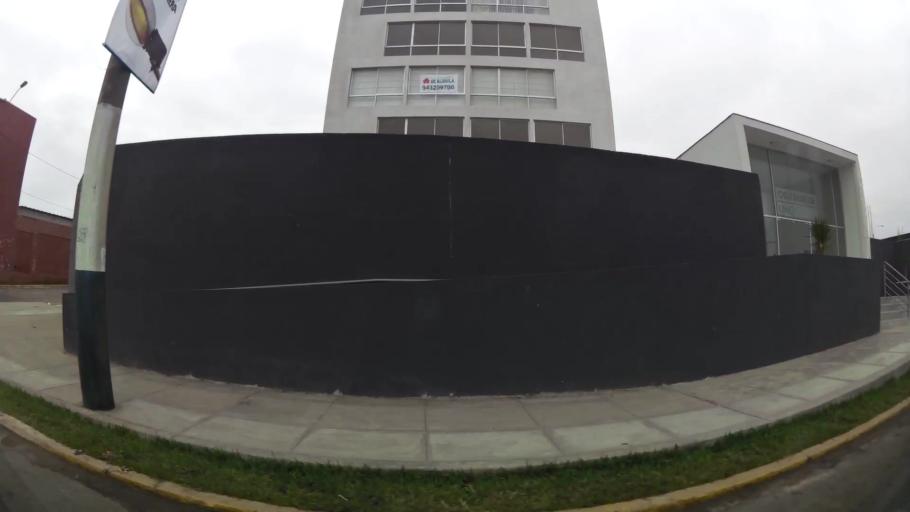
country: PE
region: Callao
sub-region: Callao
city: Callao
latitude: -12.0732
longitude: -77.1246
